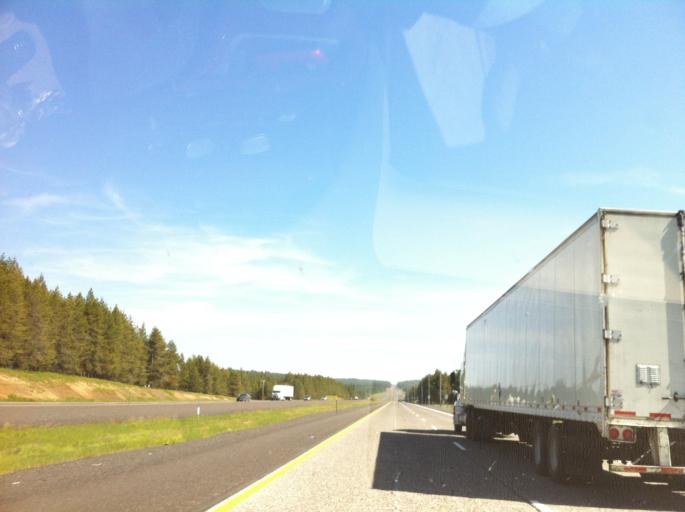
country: US
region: Oregon
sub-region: Umatilla County
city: Mission
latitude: 45.5224
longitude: -118.4409
